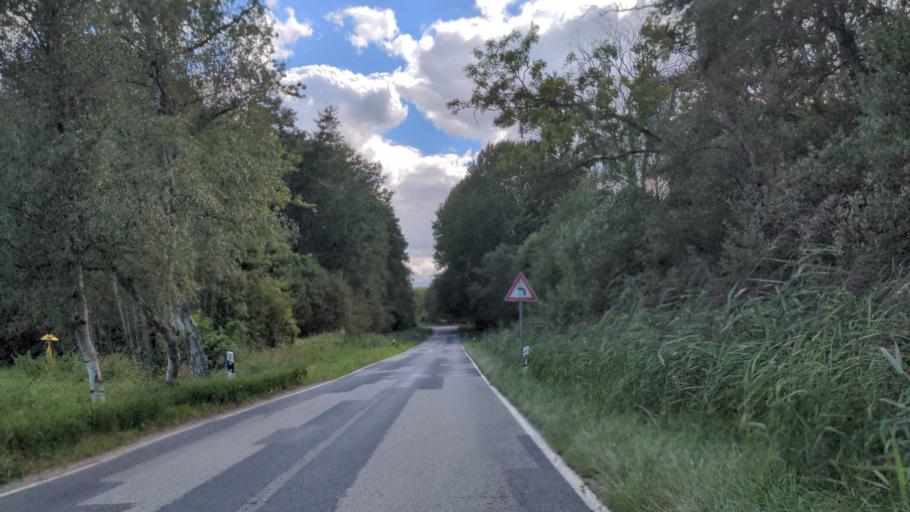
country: DE
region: Mecklenburg-Vorpommern
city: Gramkow
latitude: 53.9231
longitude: 11.3718
